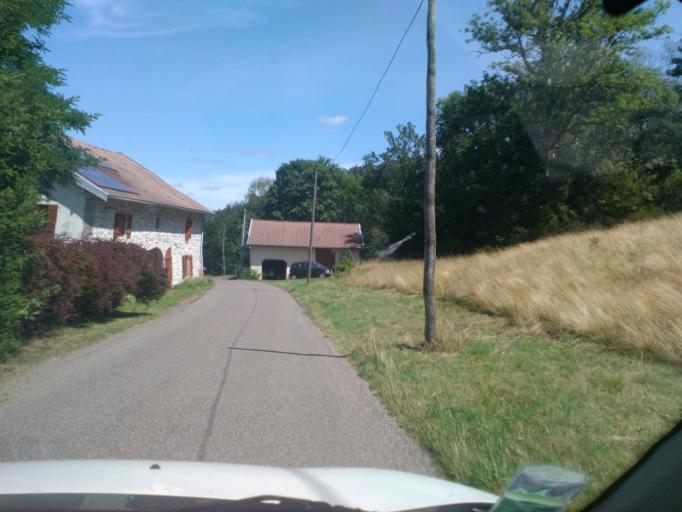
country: FR
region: Lorraine
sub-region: Departement des Vosges
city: Le Tholy
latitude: 48.0726
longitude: 6.7517
